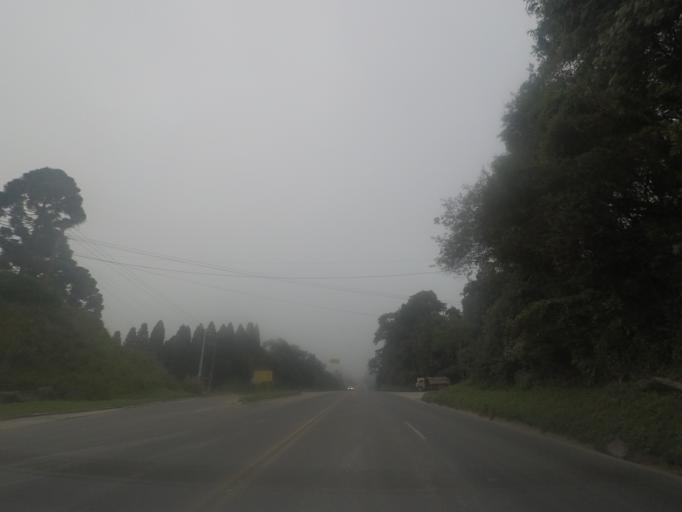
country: BR
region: Parana
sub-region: Almirante Tamandare
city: Almirante Tamandare
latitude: -25.2691
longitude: -49.3032
